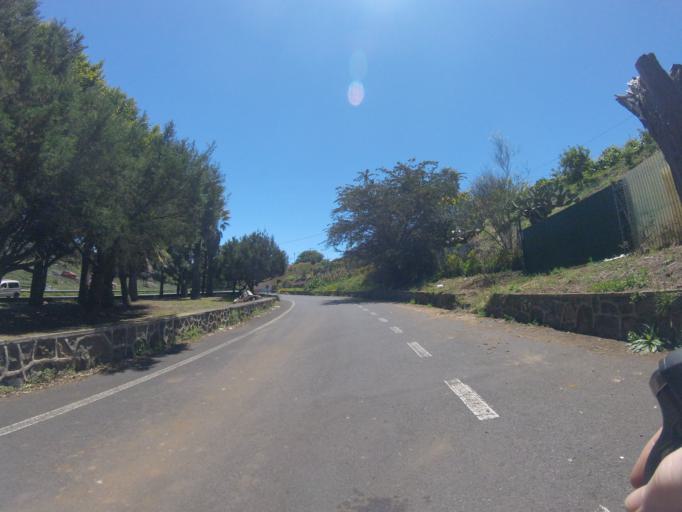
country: ES
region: Canary Islands
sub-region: Provincia de Santa Cruz de Tenerife
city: Tegueste
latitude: 28.5135
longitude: -16.3101
